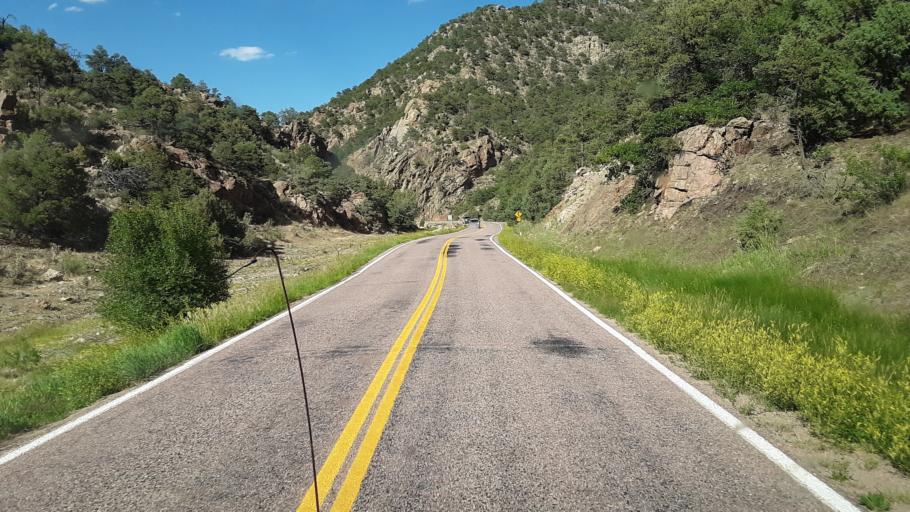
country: US
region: Colorado
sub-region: Fremont County
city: Canon City
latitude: 38.4207
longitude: -105.4089
